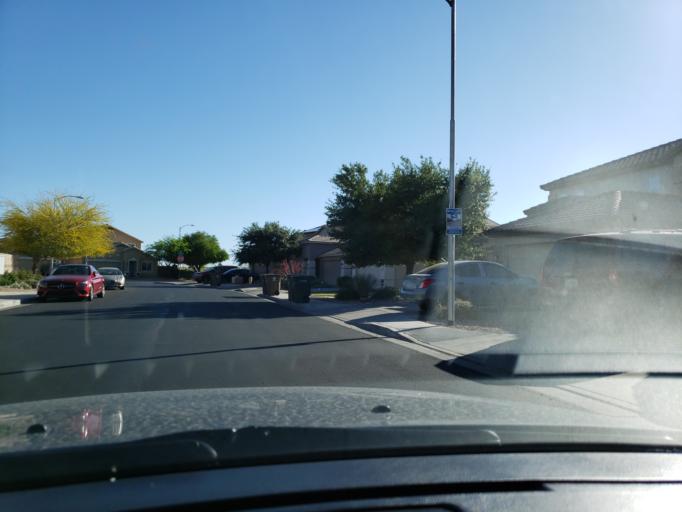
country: US
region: Arizona
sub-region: Maricopa County
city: Youngtown
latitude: 33.5786
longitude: -112.3108
